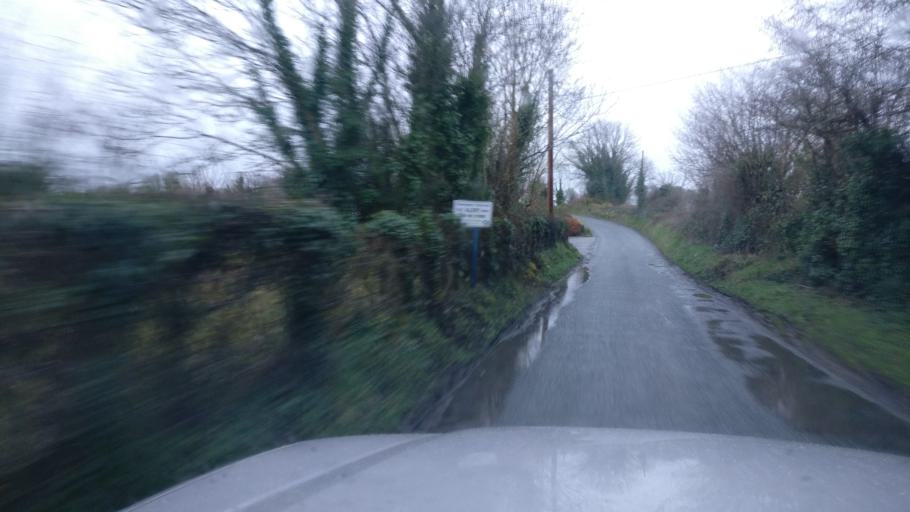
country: IE
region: Connaught
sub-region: County Galway
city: Ballinasloe
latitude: 53.3051
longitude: -8.2788
